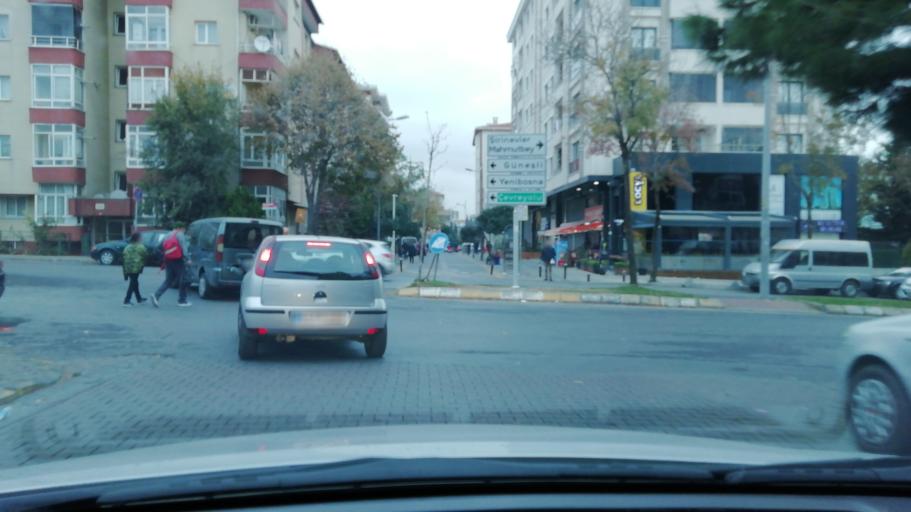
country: TR
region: Istanbul
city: Bagcilar
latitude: 41.0220
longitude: 28.8302
